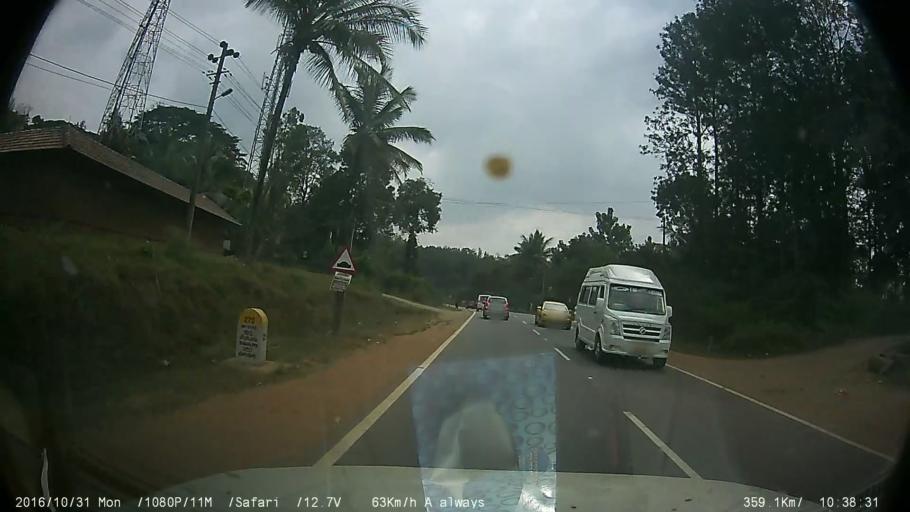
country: IN
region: Karnataka
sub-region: Kodagu
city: Suntikoppa
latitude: 12.4411
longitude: 75.8713
